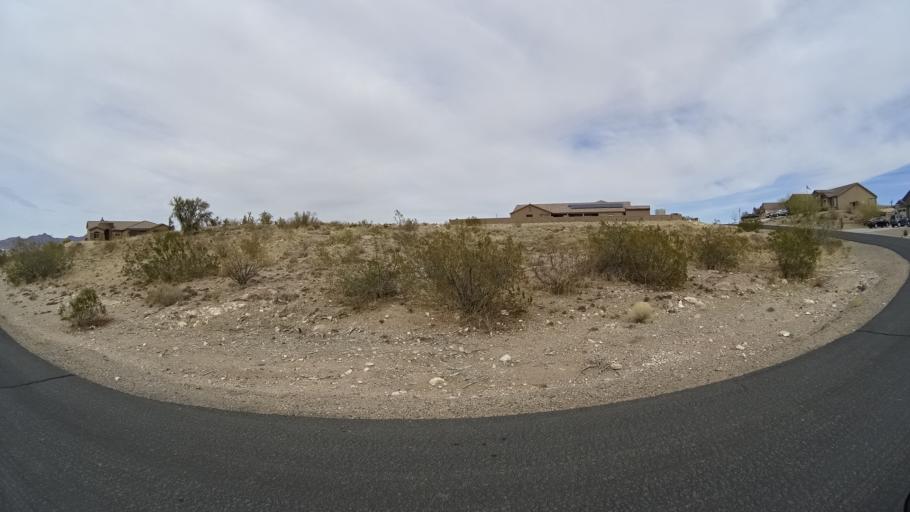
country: US
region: Arizona
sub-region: Mohave County
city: Kingman
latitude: 35.1753
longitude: -113.9958
